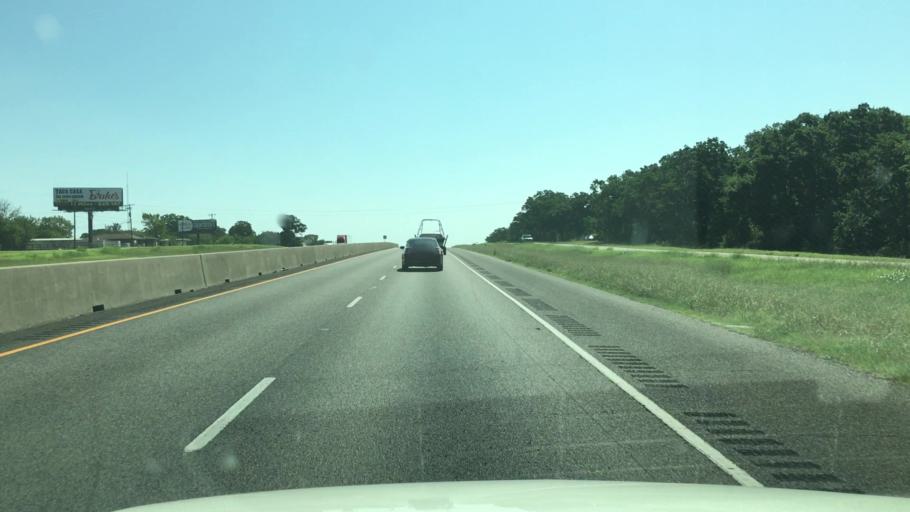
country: US
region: Texas
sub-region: Hopkins County
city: Sulphur Springs
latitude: 33.1470
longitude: -95.5422
